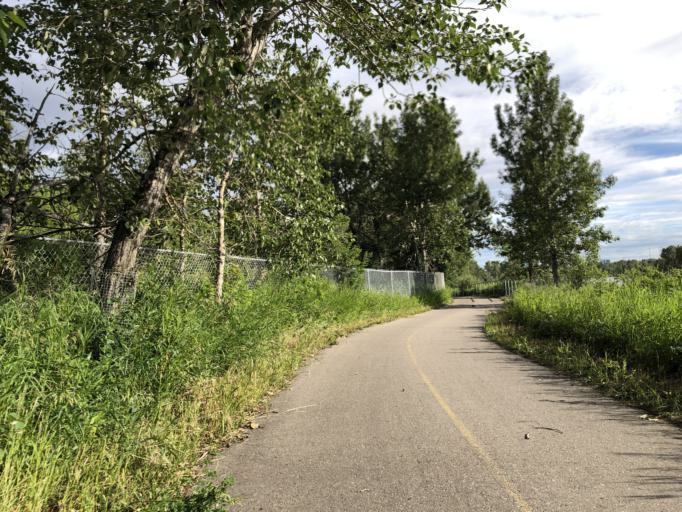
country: CA
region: Alberta
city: Calgary
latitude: 51.0173
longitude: -114.0128
